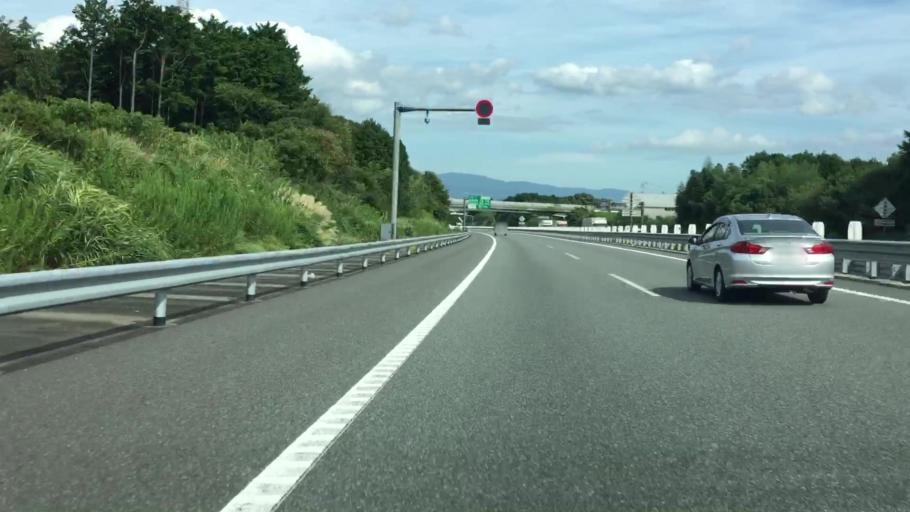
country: JP
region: Shizuoka
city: Numazu
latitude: 35.1522
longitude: 138.8466
